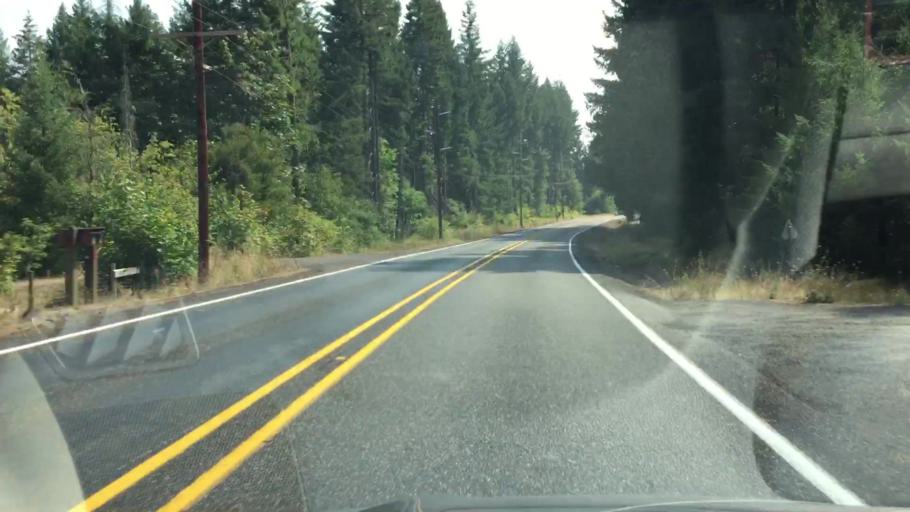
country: US
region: Washington
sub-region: Klickitat County
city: White Salmon
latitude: 45.8656
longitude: -121.5109
